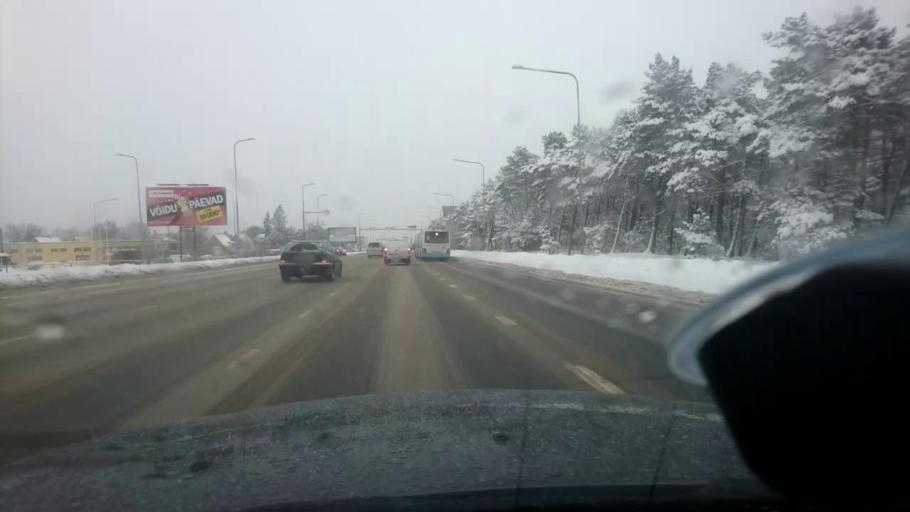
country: EE
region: Harju
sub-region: Tallinna linn
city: Tallinn
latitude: 59.3970
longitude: 24.7264
